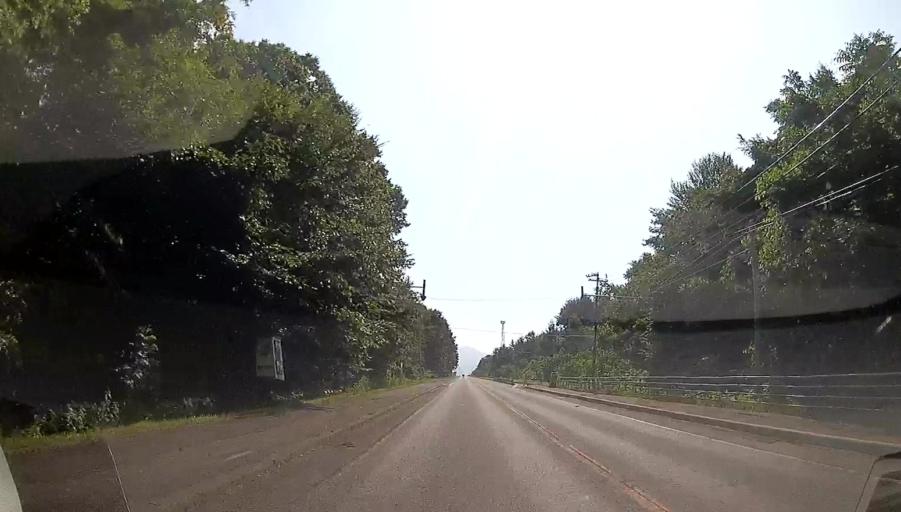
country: JP
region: Hokkaido
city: Otofuke
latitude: 43.0047
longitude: 142.8727
